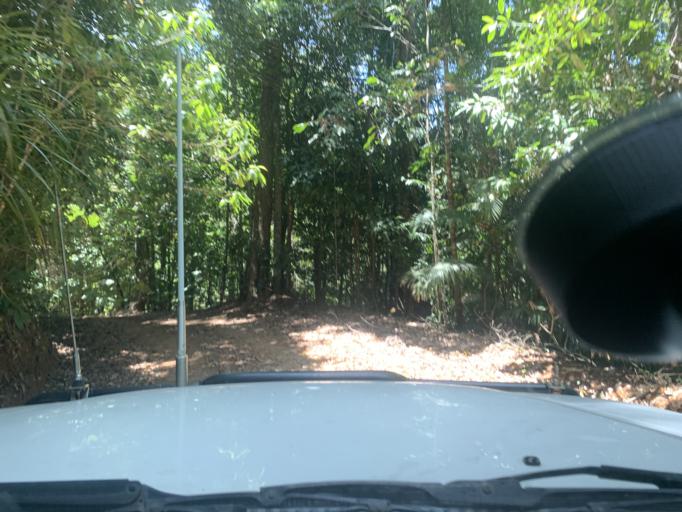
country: AU
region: Queensland
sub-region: Cairns
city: Woree
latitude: -16.9742
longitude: 145.6503
